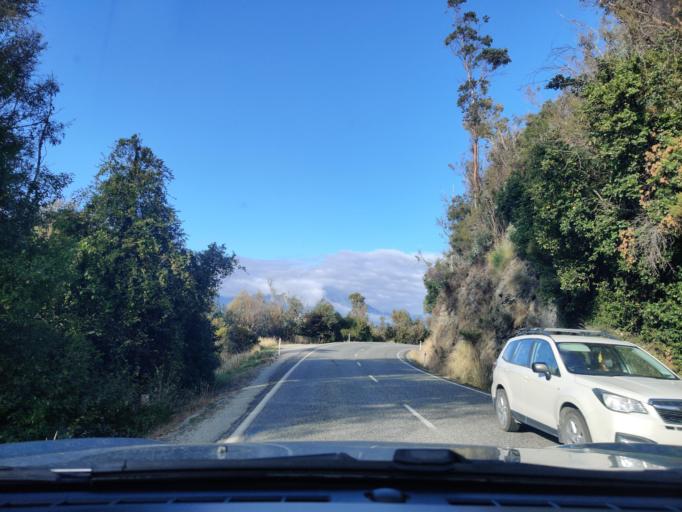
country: NZ
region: Otago
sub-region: Queenstown-Lakes District
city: Queenstown
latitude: -45.0456
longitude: 168.6309
